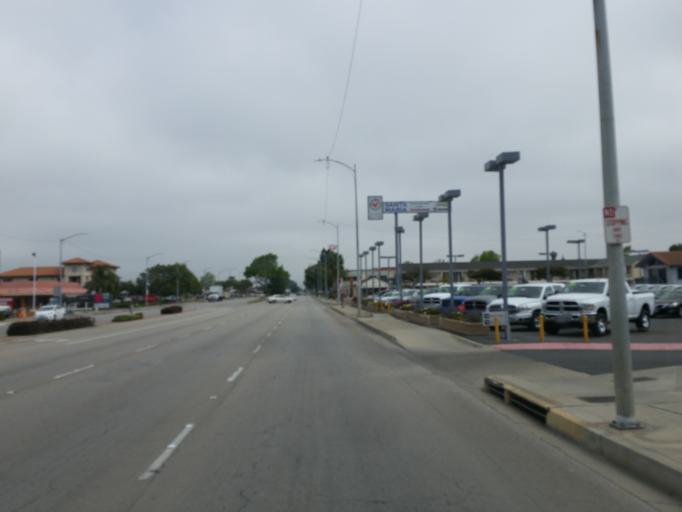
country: US
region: California
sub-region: Santa Barbara County
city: Santa Maria
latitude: 34.9256
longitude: -120.4359
